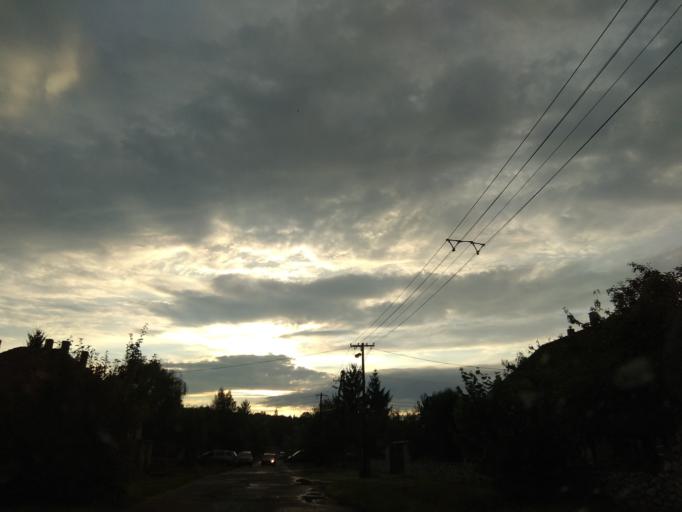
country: HU
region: Borsod-Abauj-Zemplen
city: Miskolc
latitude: 48.0595
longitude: 20.7882
